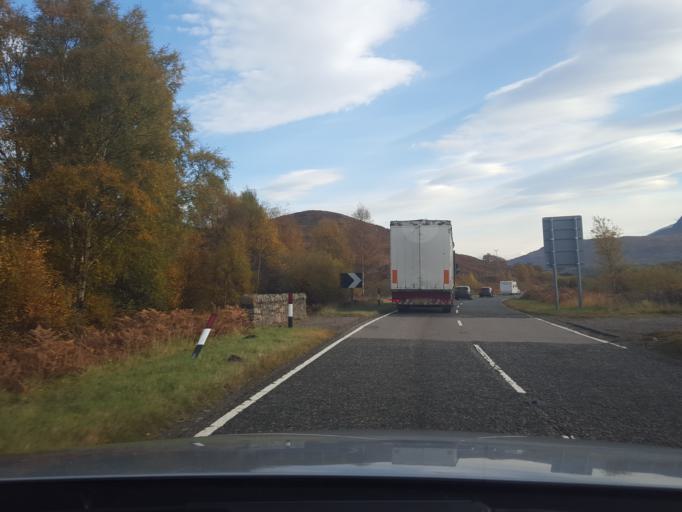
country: GB
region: Scotland
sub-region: Highland
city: Spean Bridge
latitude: 57.1456
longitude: -4.9761
